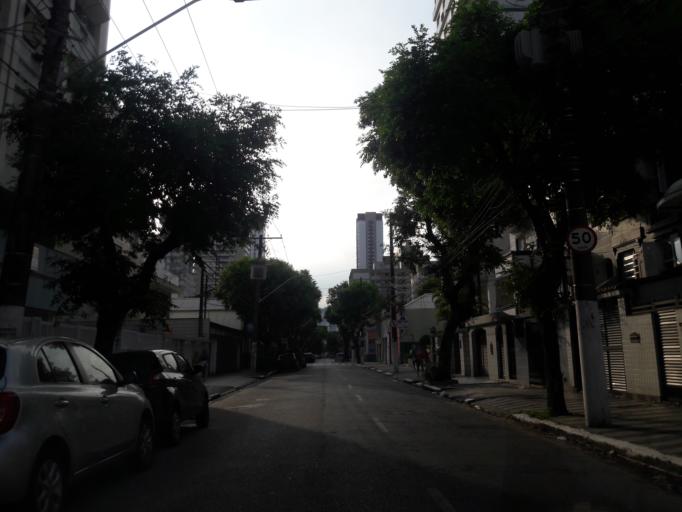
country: BR
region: Sao Paulo
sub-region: Santos
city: Santos
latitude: -23.9654
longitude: -46.3392
